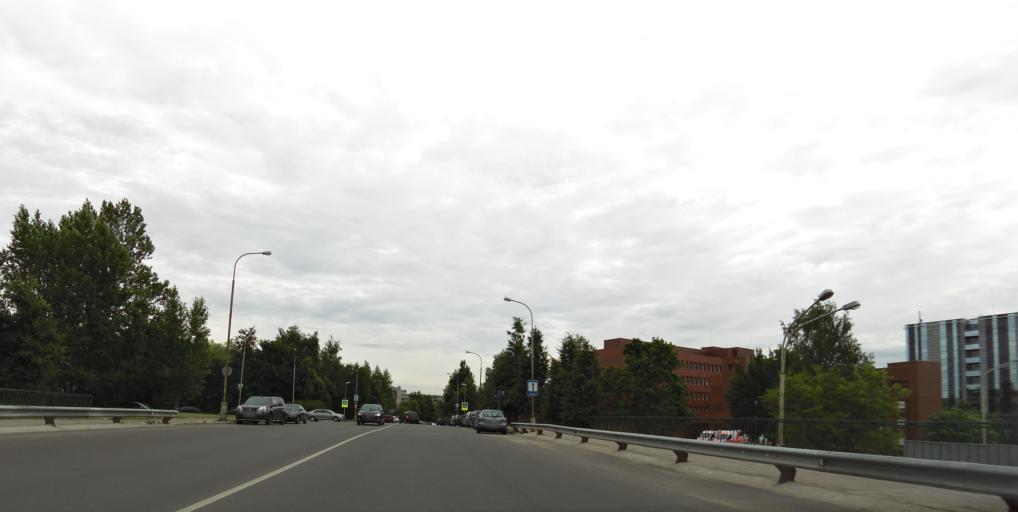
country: LT
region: Vilnius County
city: Seskine
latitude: 54.7167
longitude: 25.2468
